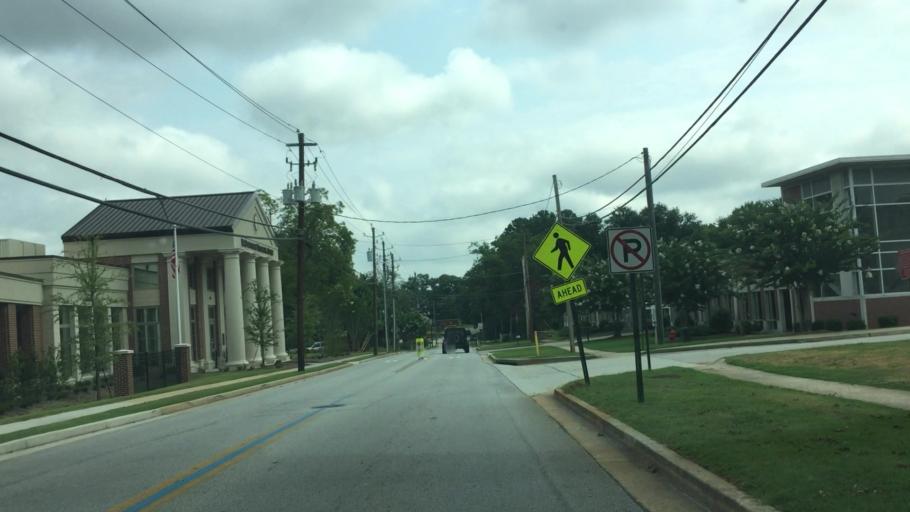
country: US
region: Georgia
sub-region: Henry County
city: McDonough
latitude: 33.4490
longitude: -84.1457
